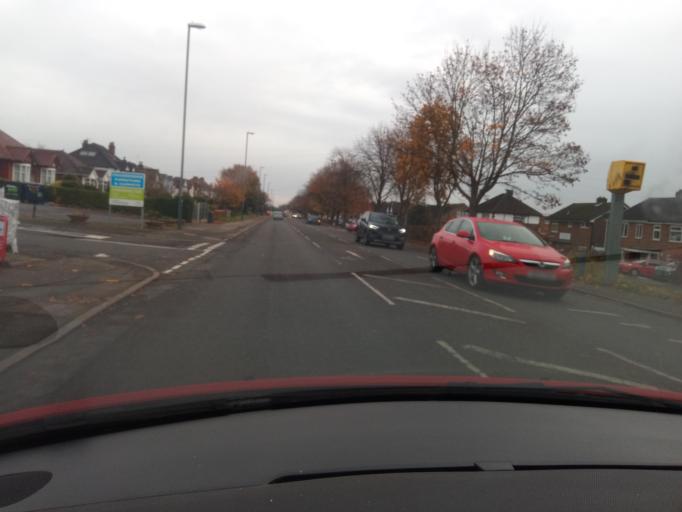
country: GB
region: England
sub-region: Derbyshire
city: Borrowash
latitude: 52.9206
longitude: -1.4290
